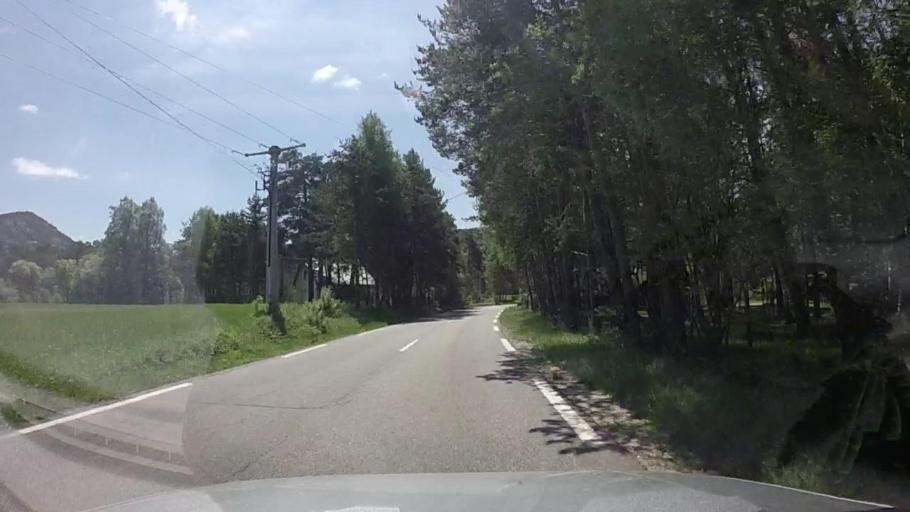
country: FR
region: Provence-Alpes-Cote d'Azur
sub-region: Departement des Alpes-de-Haute-Provence
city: Seyne-les-Alpes
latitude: 44.3790
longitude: 6.3270
